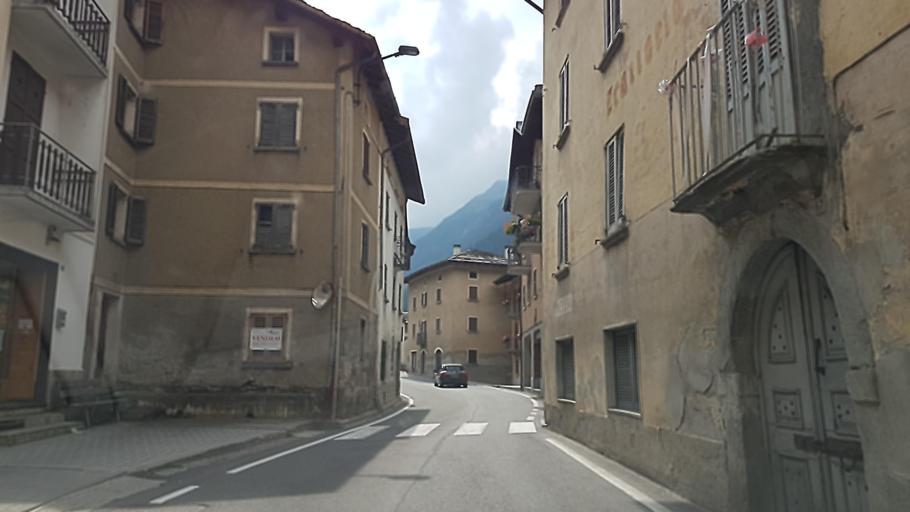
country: IT
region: Lombardy
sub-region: Provincia di Sondrio
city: Campodolcino
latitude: 46.4060
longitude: 9.3519
